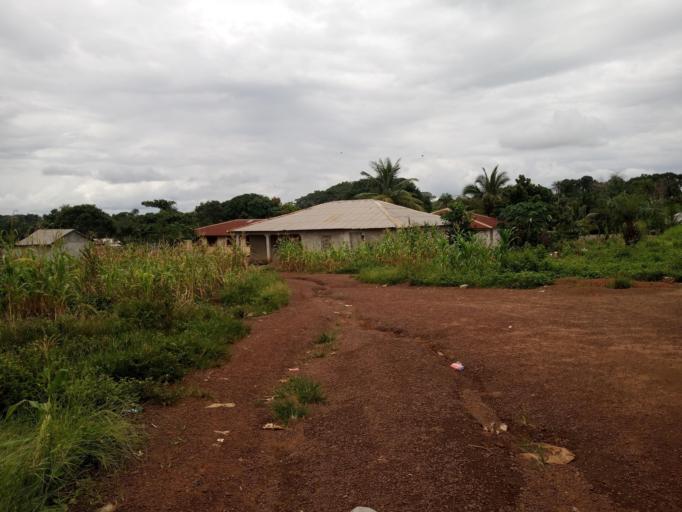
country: SL
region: Northern Province
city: Kamakwie
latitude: 9.5028
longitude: -12.2529
